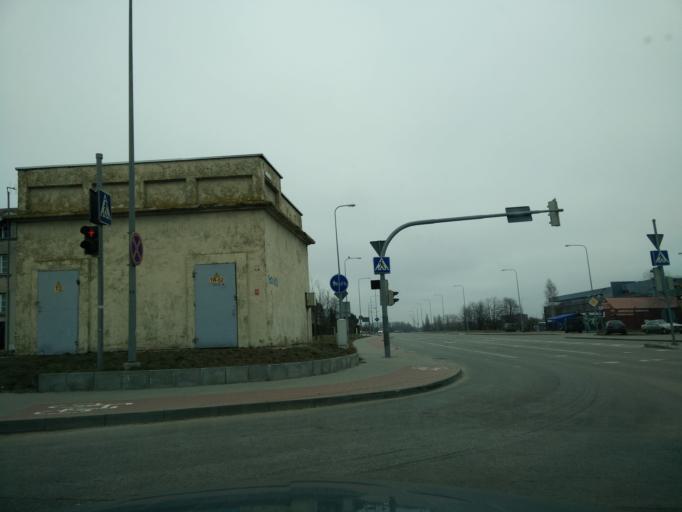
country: LT
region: Klaipedos apskritis
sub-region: Klaipeda
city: Klaipeda
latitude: 55.6874
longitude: 21.1460
